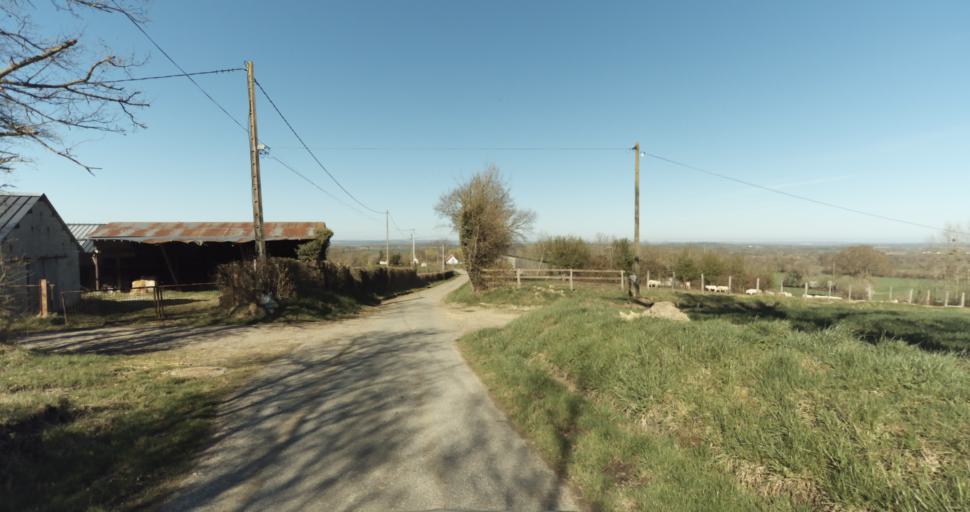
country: FR
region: Lower Normandy
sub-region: Departement de l'Orne
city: Trun
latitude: 48.9130
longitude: 0.0518
